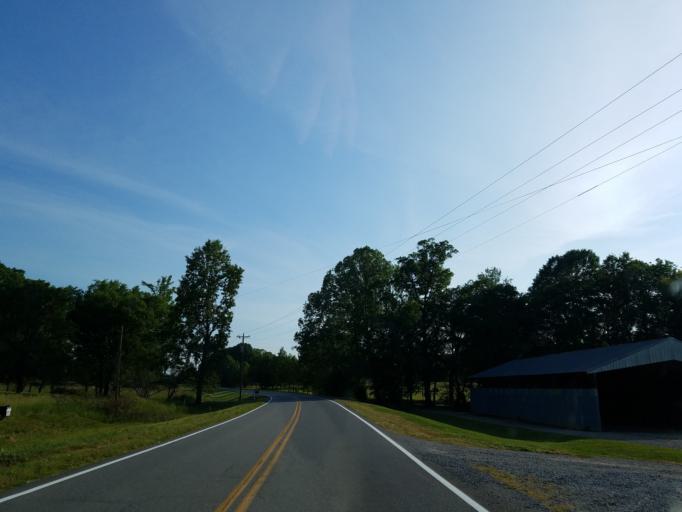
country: US
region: Georgia
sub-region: Chattooga County
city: Trion
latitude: 34.4812
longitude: -85.2599
